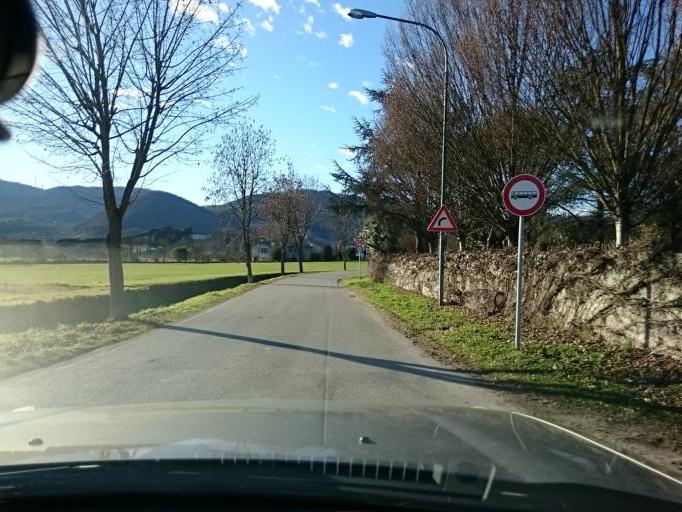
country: IT
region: Veneto
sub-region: Provincia di Padova
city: Torreglia
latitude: 45.3412
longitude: 11.7281
